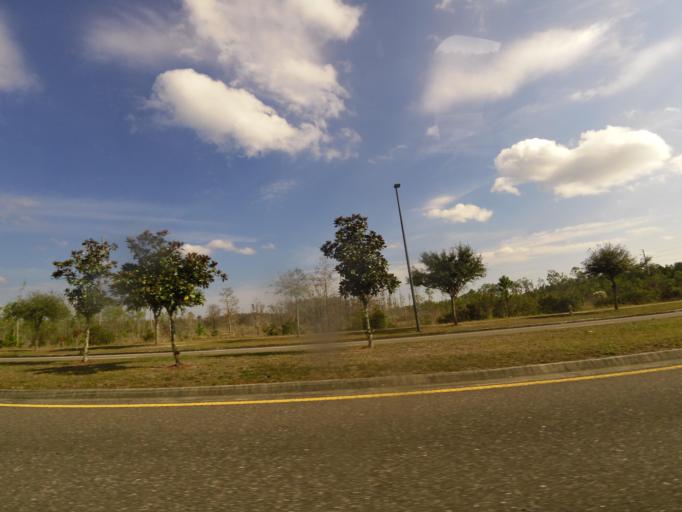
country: US
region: Florida
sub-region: Duval County
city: Baldwin
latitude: 30.2618
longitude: -81.8866
